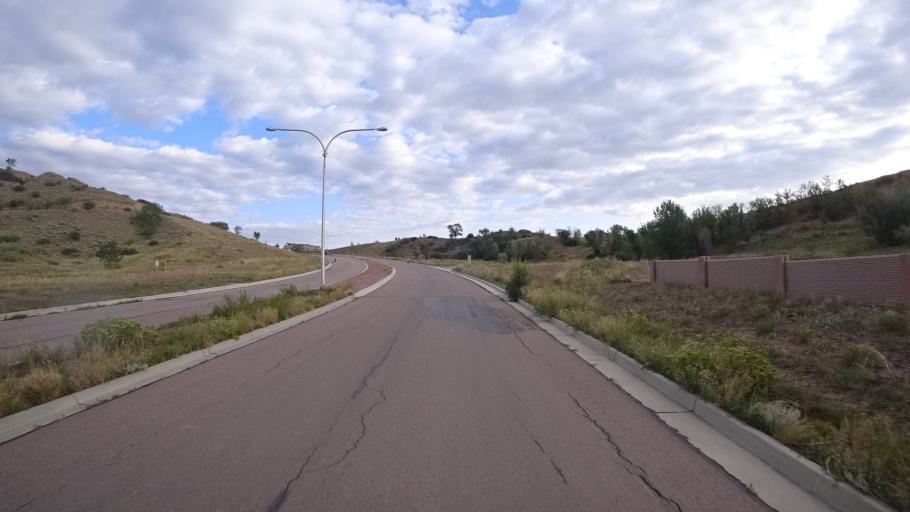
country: US
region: Colorado
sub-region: El Paso County
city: Colorado Springs
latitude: 38.8707
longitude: -104.8423
